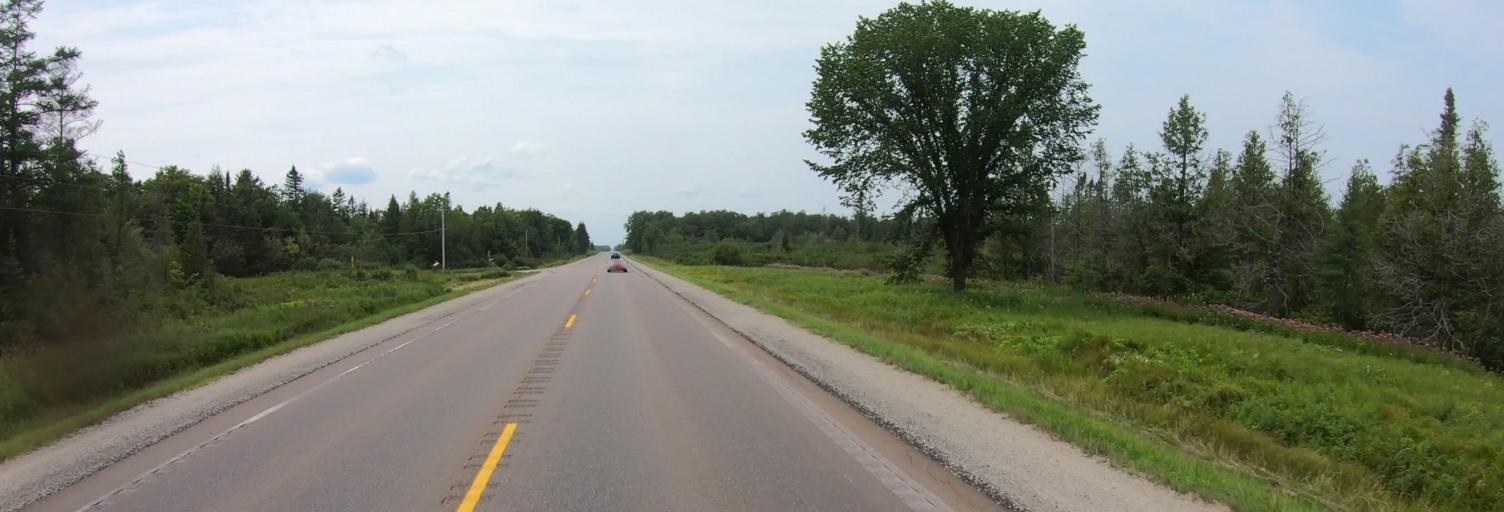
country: US
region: Michigan
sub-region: Marquette County
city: K. I. Sawyer Air Force Base
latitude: 46.3476
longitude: -87.0684
